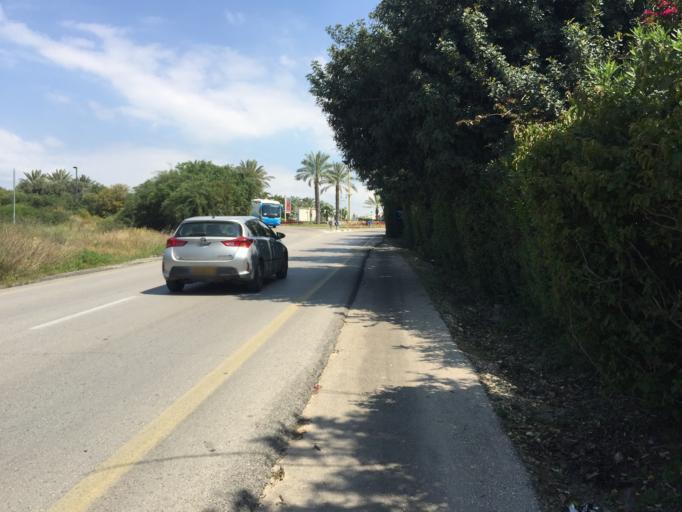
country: IL
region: Haifa
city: Qesarya
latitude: 32.4901
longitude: 34.9024
